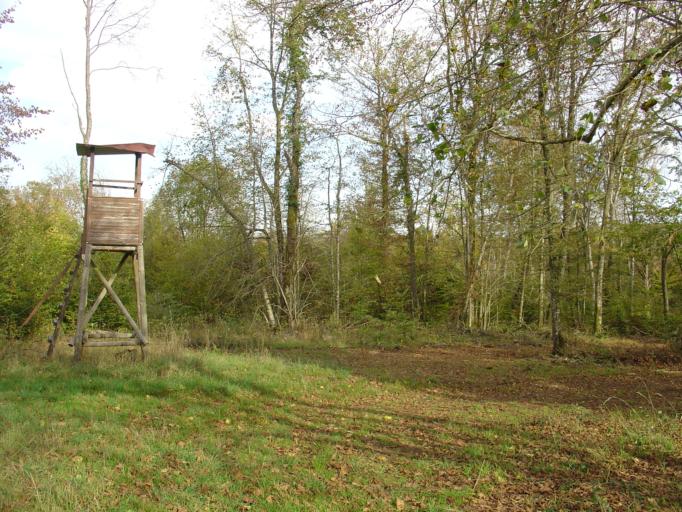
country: FR
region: Lorraine
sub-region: Departement de Meurthe-et-Moselle
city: Saizerais
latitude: 48.8291
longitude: 5.9668
